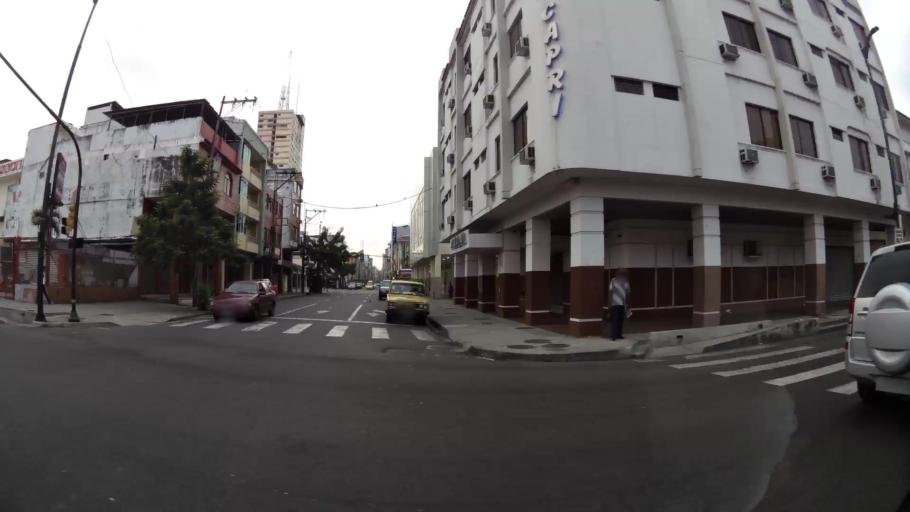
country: EC
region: Guayas
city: Guayaquil
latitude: -2.1913
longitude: -79.8904
